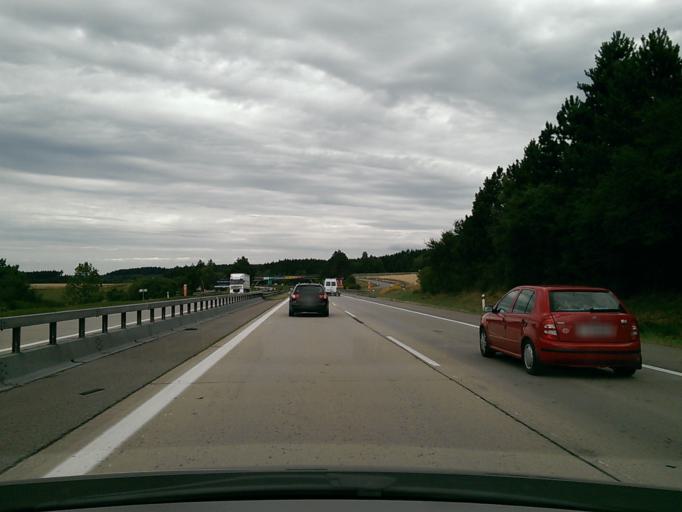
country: CZ
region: Vysocina
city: Velky Beranov
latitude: 49.4175
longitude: 15.7052
